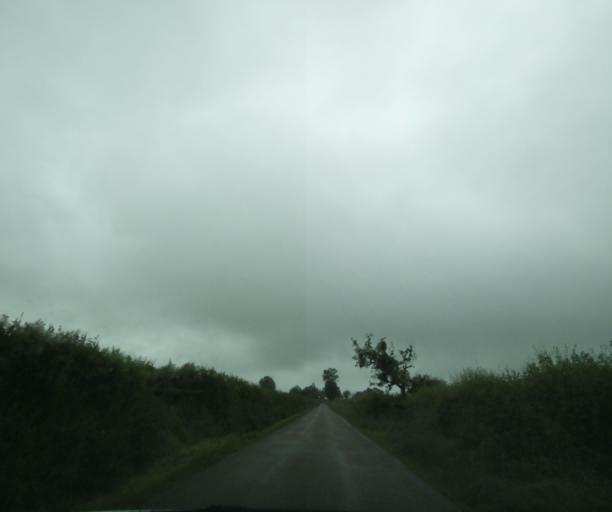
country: FR
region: Bourgogne
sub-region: Departement de Saone-et-Loire
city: Charolles
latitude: 46.3637
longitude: 4.2141
